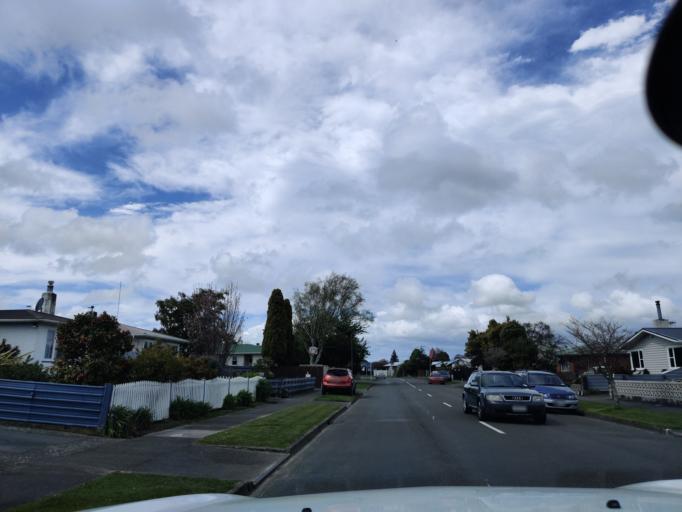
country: NZ
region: Manawatu-Wanganui
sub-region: Palmerston North City
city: Palmerston North
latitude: -40.3604
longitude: 175.5829
